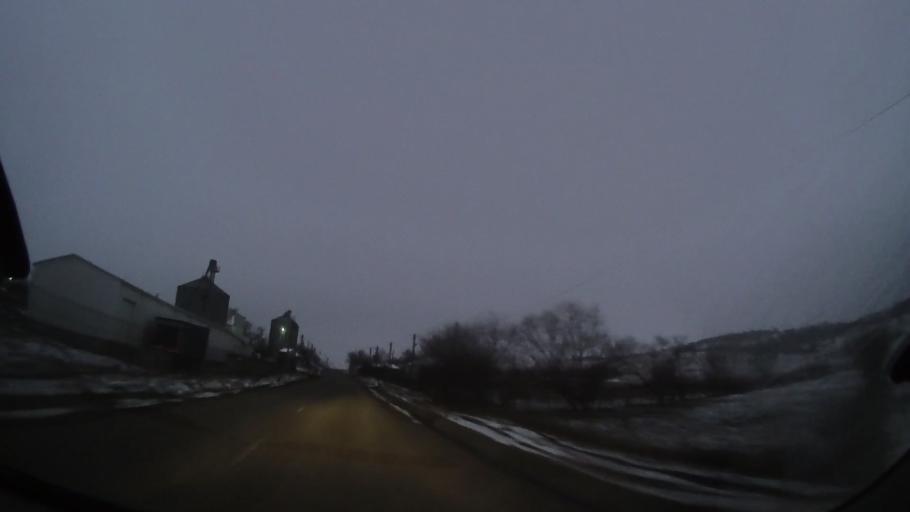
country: RO
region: Vaslui
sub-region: Comuna Dimitrie Cantemir
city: Dimitrie Cantemir
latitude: 46.4982
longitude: 28.0529
